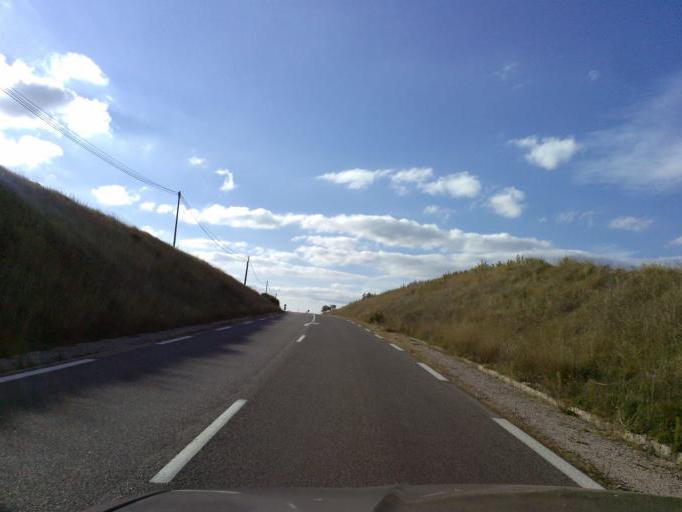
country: FR
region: Provence-Alpes-Cote d'Azur
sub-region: Departement des Alpes-de-Haute-Provence
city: Valensole
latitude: 43.8381
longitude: 5.9643
